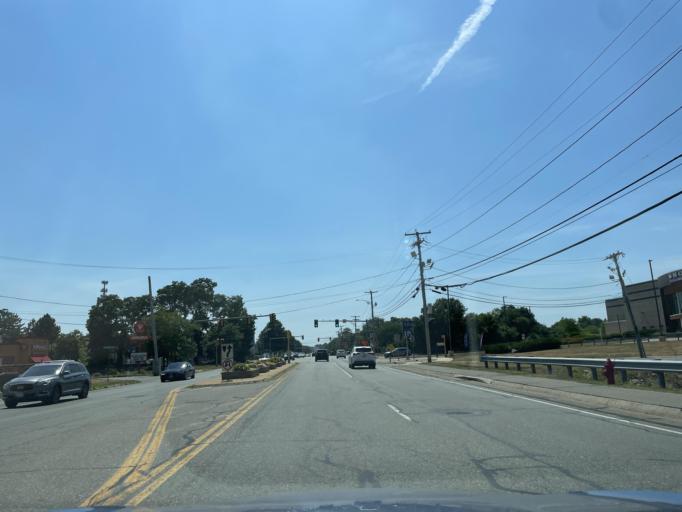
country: US
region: Massachusetts
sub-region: Norfolk County
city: Randolph
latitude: 42.1632
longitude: -71.0602
